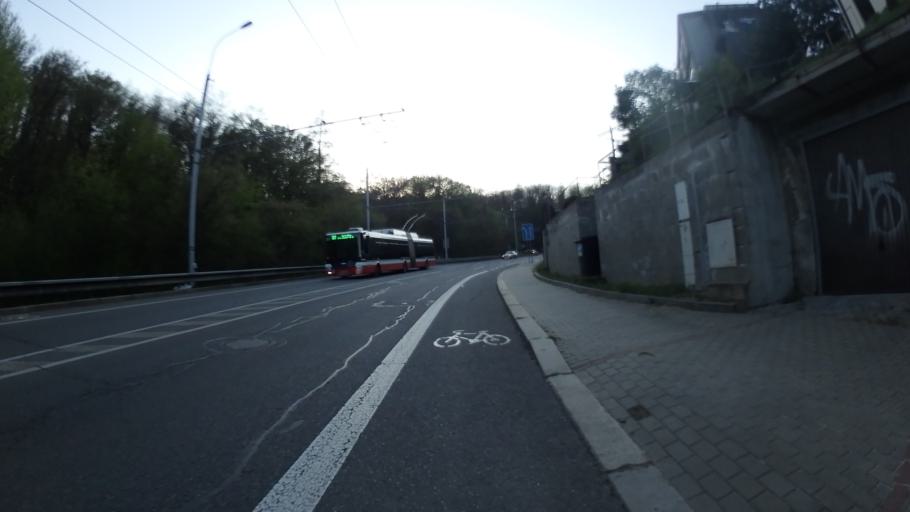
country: CZ
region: South Moravian
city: Ostopovice
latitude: 49.1946
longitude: 16.5572
